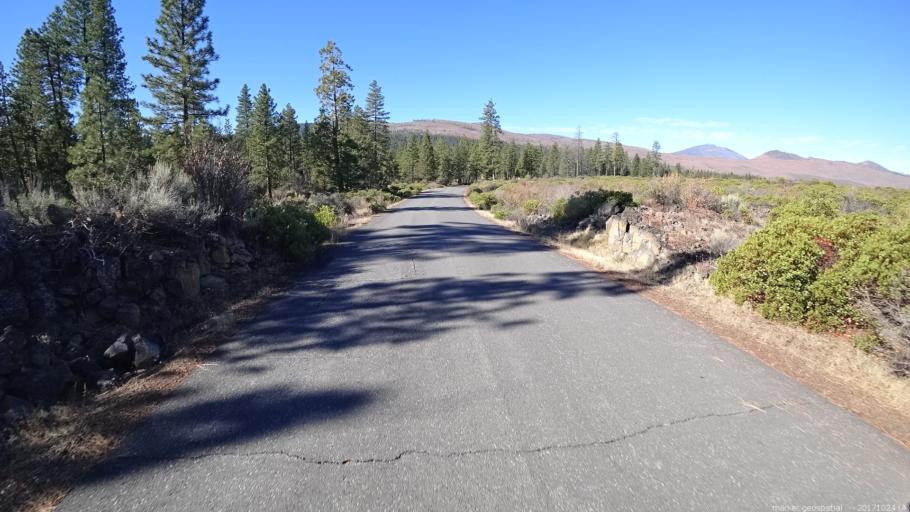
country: US
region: California
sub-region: Shasta County
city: Burney
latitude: 40.7490
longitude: -121.4675
